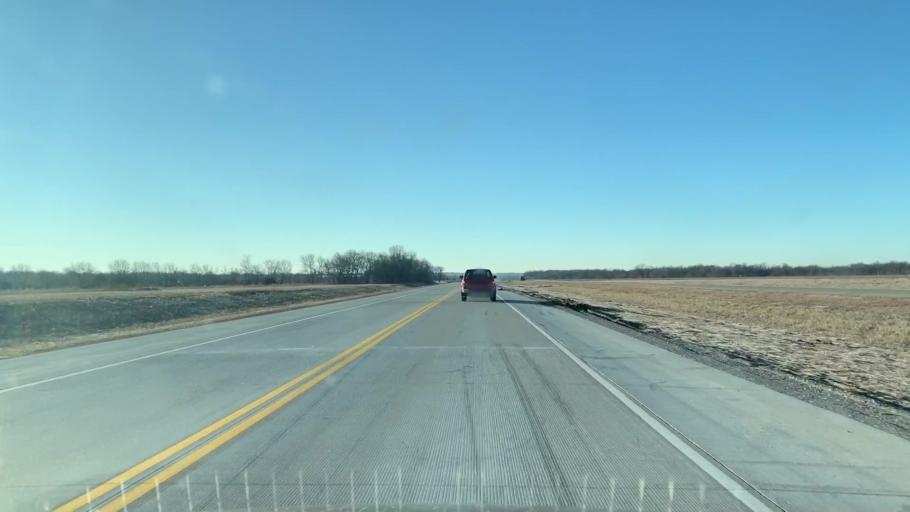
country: US
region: Kansas
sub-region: Bourbon County
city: Fort Scott
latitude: 37.7234
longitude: -94.7043
